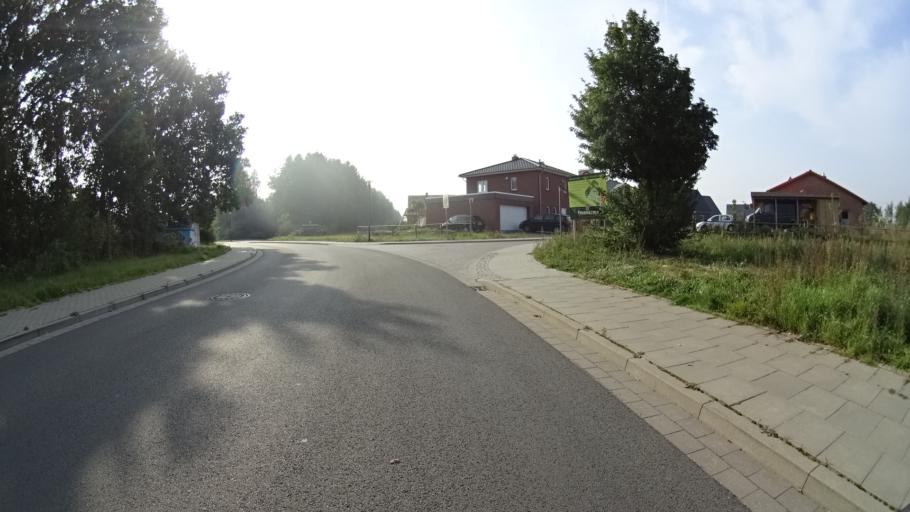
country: DE
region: Lower Saxony
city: Reppenstedt
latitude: 53.2262
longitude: 10.3727
